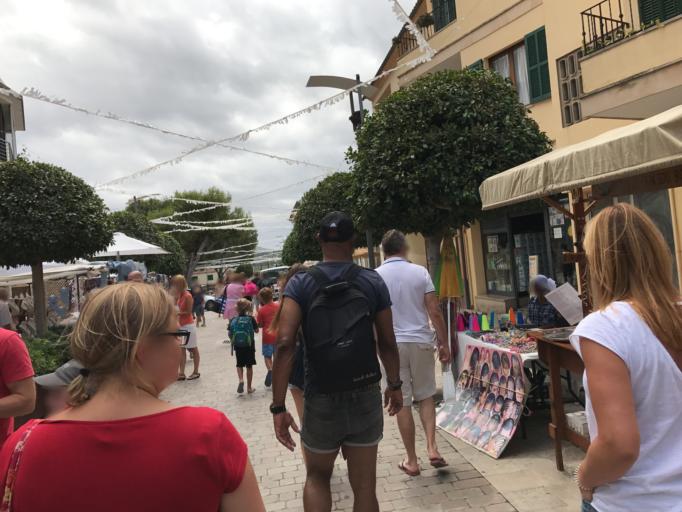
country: ES
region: Balearic Islands
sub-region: Illes Balears
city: Arta
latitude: 39.6919
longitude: 3.3489
